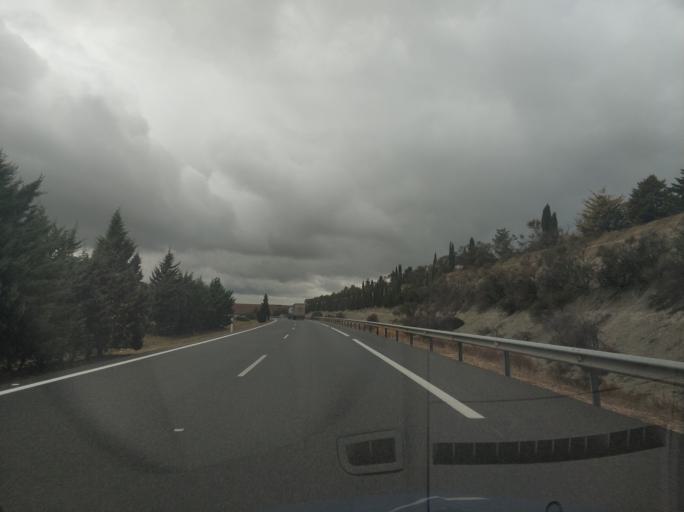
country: ES
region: Castille and Leon
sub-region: Provincia de Palencia
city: Soto de Cerrato
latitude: 41.9696
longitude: -4.4550
